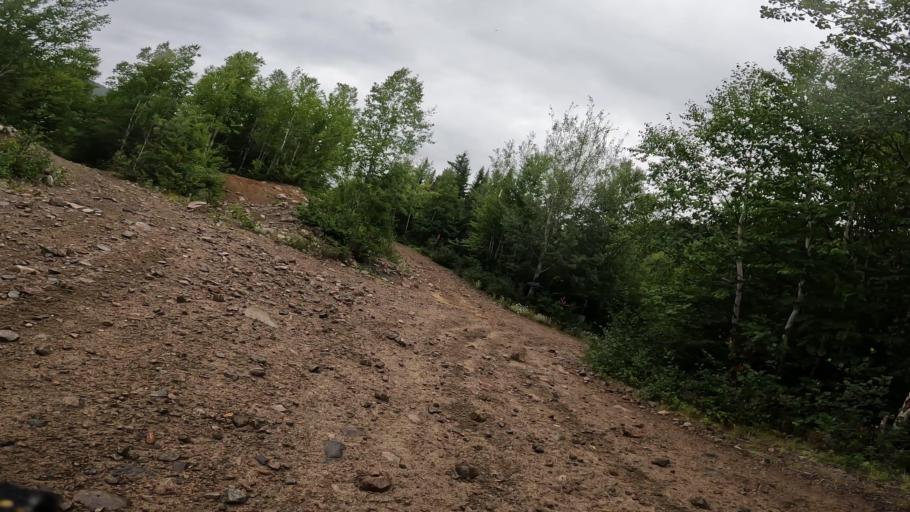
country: CA
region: Quebec
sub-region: Capitale-Nationale
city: Baie-Saint-Paul
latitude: 47.7884
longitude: -70.4890
